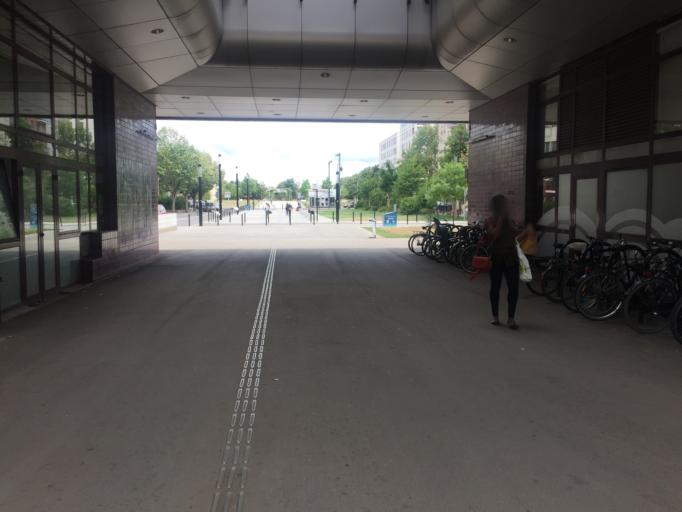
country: FR
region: Ile-de-France
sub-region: Departement des Yvelines
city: Montigny-le-Bretonneux
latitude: 48.7864
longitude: 2.0454
